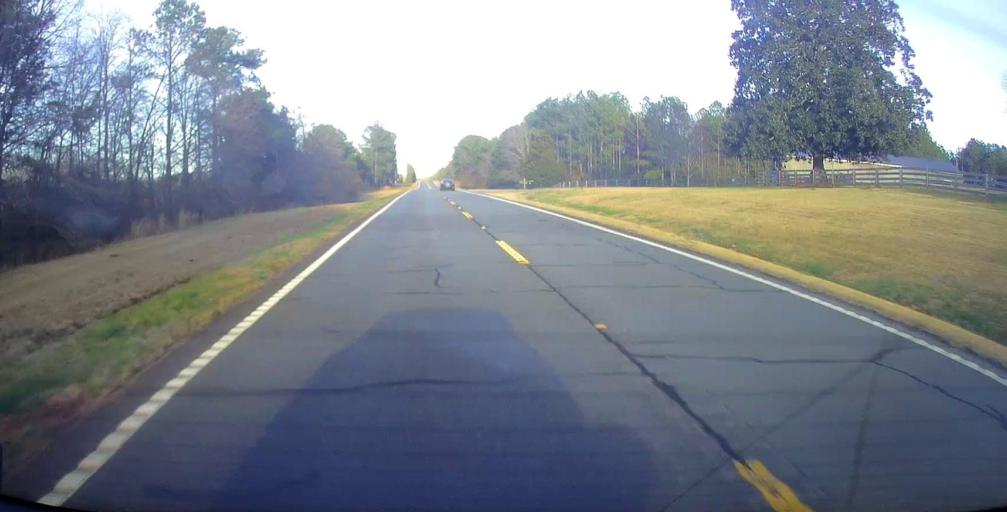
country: US
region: Georgia
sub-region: Talbot County
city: Talbotton
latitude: 32.7863
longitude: -84.5184
